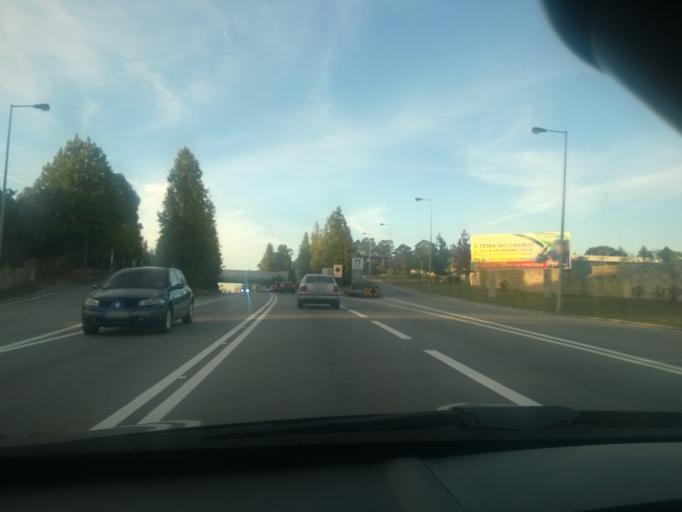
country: PT
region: Porto
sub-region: Maia
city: Maia
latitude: 41.2254
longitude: -8.6263
